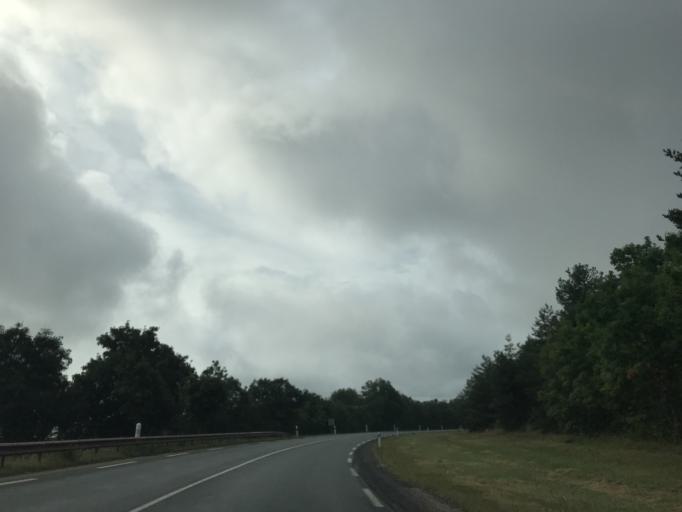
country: FR
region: Auvergne
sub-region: Departement de la Haute-Loire
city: Polignac
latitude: 45.0759
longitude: 3.8436
